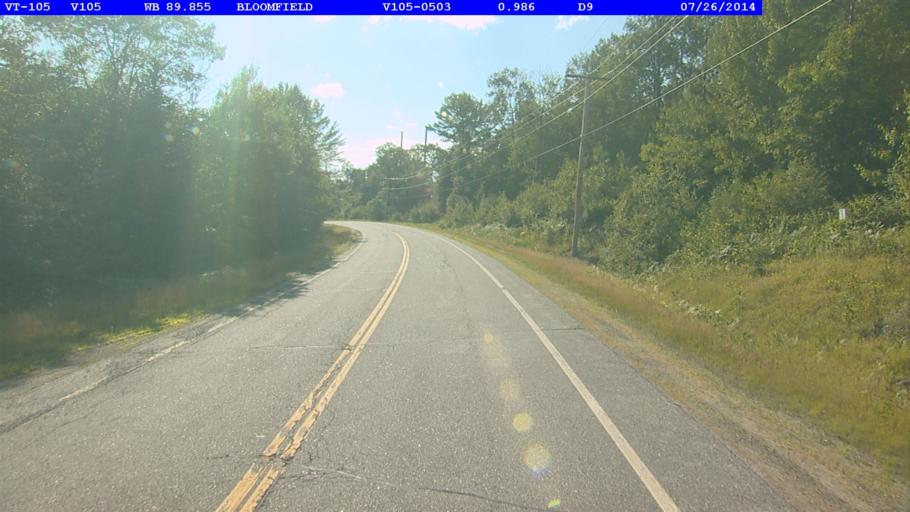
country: US
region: New Hampshire
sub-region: Coos County
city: Stratford
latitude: 44.7797
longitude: -71.6718
